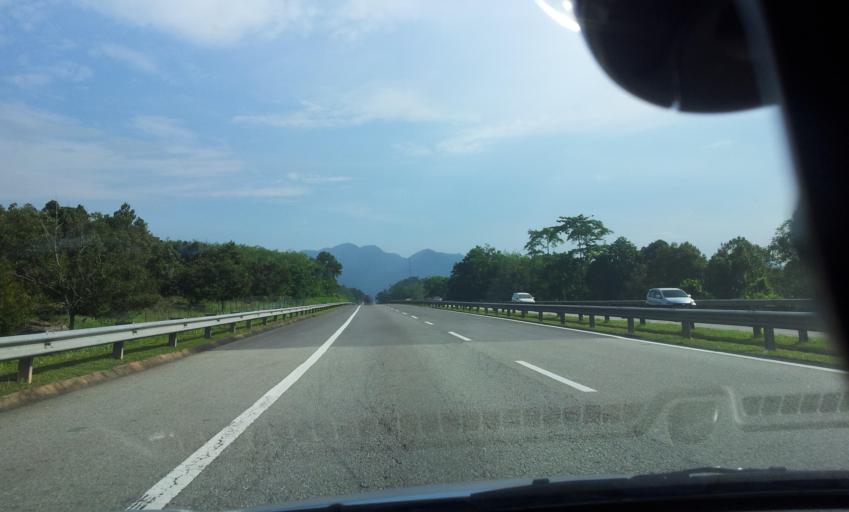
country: MY
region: Pahang
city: Bentong Town
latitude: 3.4639
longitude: 102.0447
